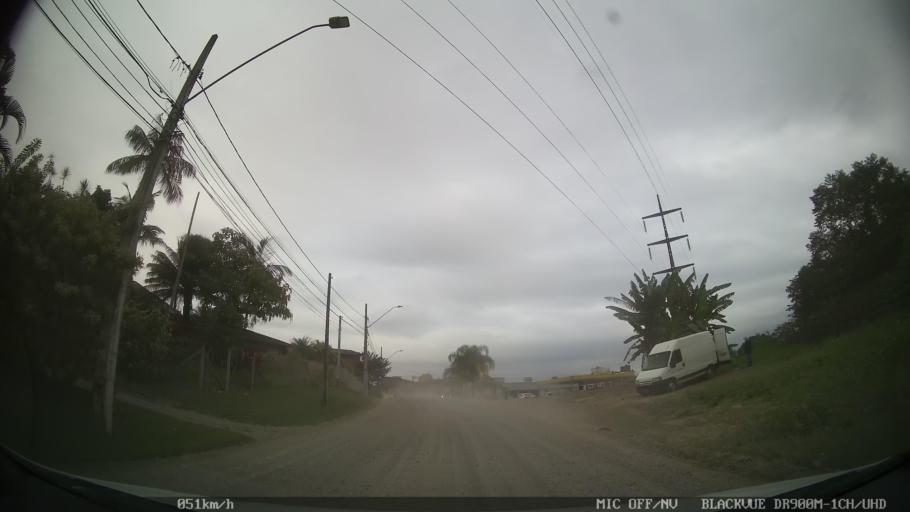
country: BR
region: Santa Catarina
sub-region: Joinville
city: Joinville
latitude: -26.2737
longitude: -48.8675
